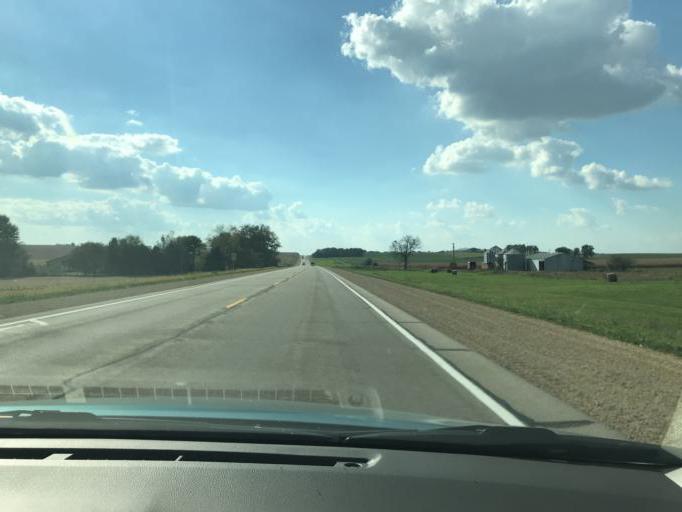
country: US
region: Wisconsin
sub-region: Green County
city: Brodhead
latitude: 42.5883
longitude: -89.4289
